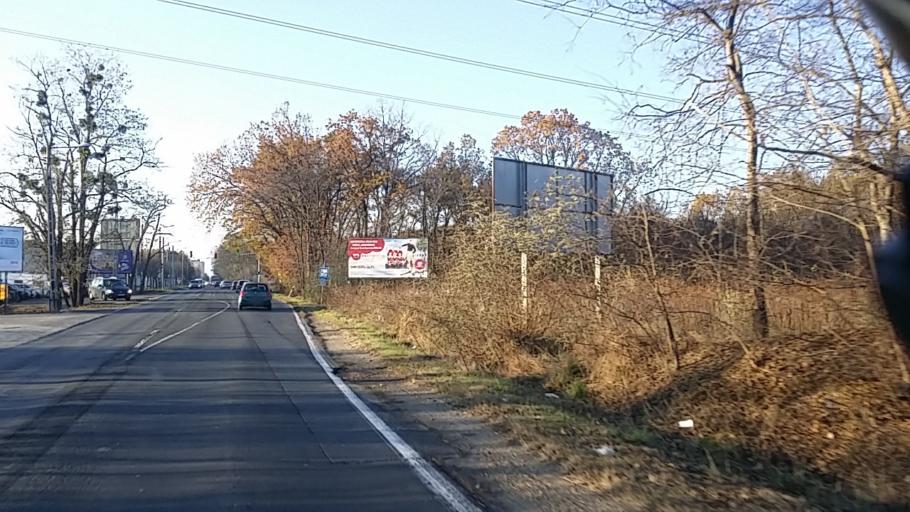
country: HU
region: Budapest
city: Budapest XVI. keruelet
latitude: 47.5408
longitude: 19.1538
